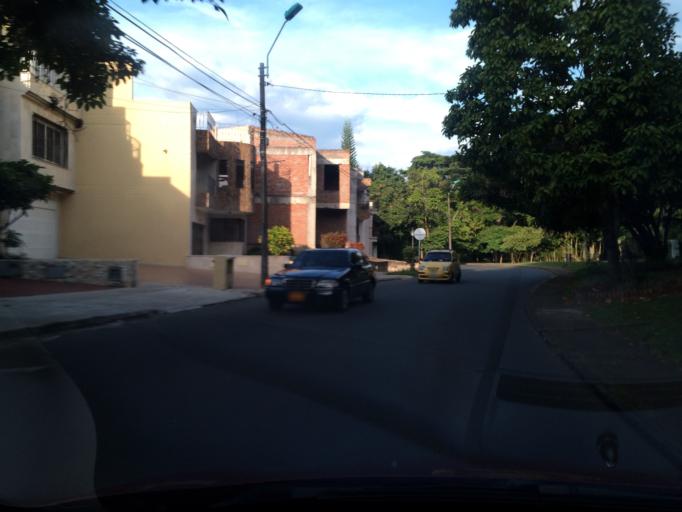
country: CO
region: Valle del Cauca
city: Cali
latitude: 3.3683
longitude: -76.5399
